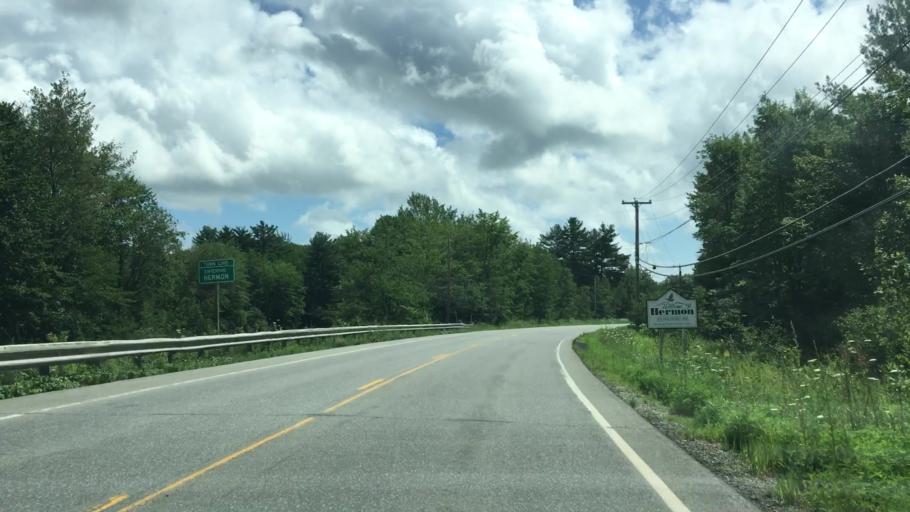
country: US
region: Maine
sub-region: Penobscot County
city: Hermon
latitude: 44.8079
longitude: -68.9720
